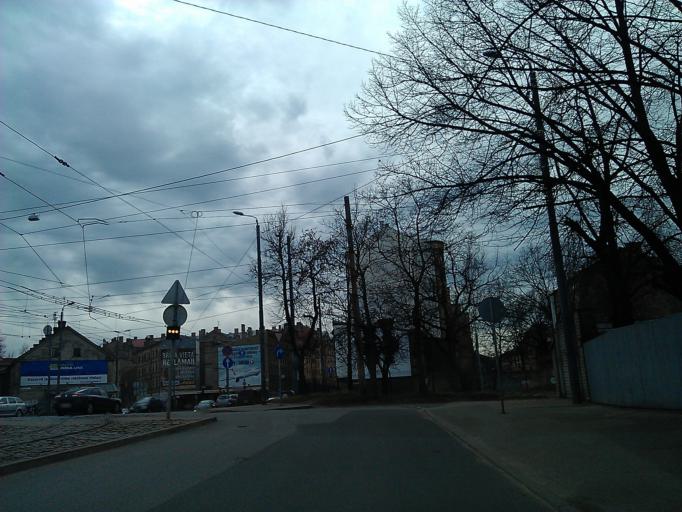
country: LV
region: Riga
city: Riga
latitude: 56.9689
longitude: 24.1522
